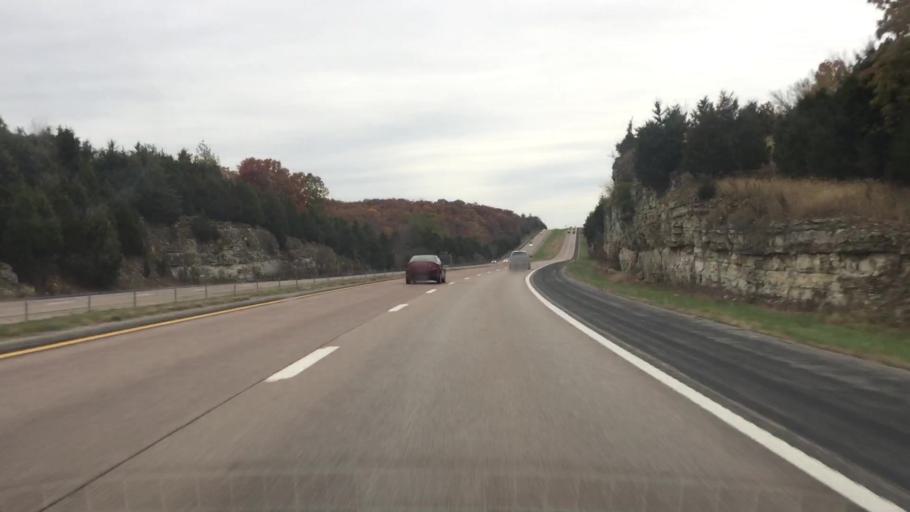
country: US
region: Missouri
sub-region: Boone County
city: Ashland
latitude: 38.6845
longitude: -92.2550
